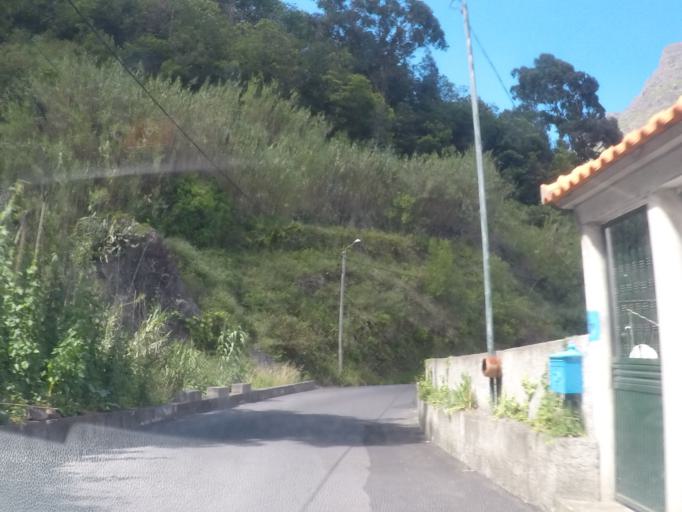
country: PT
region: Madeira
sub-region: Camara de Lobos
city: Curral das Freiras
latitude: 32.7113
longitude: -16.9737
